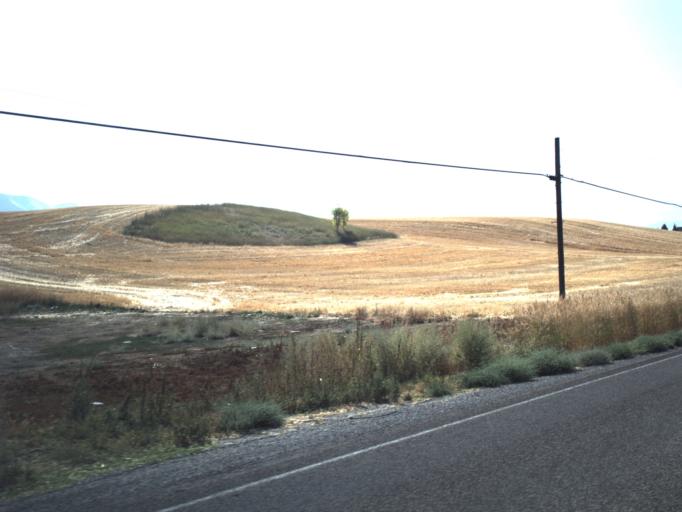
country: US
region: Utah
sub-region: Cache County
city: Hyrum
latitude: 41.5858
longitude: -111.8381
